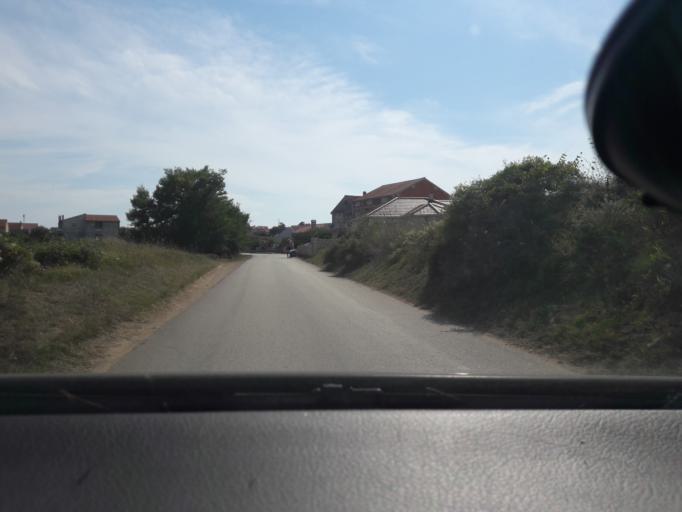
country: HR
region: Zadarska
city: Nin
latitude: 44.2447
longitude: 15.1750
